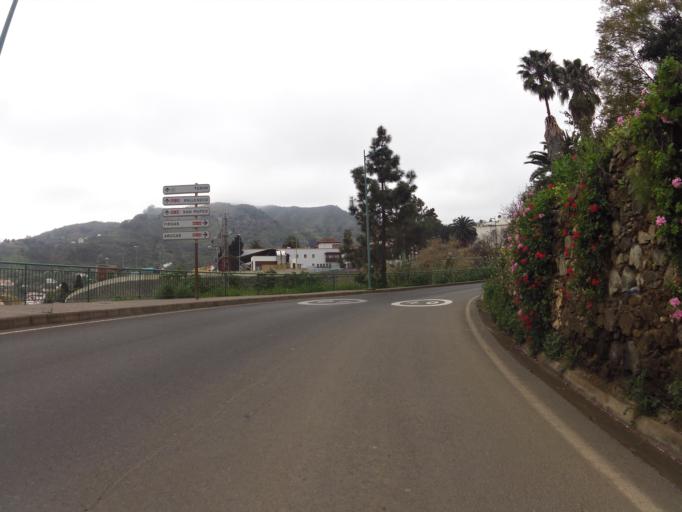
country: ES
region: Canary Islands
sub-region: Provincia de Las Palmas
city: Teror
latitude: 28.0620
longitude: -15.5440
